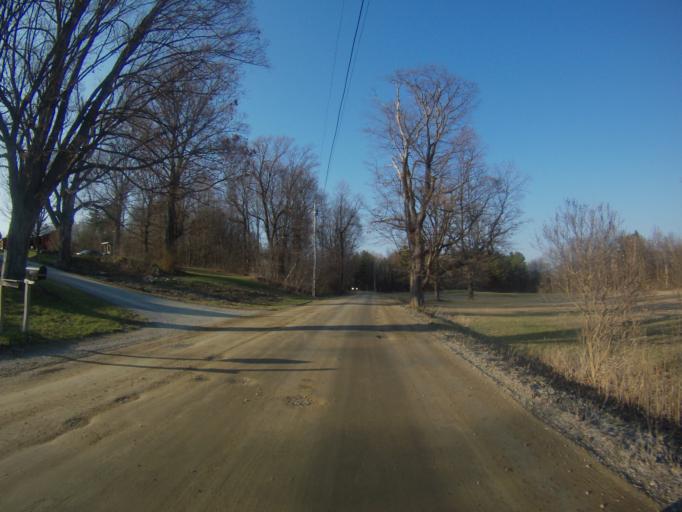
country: US
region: Vermont
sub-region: Addison County
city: Middlebury (village)
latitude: 44.0502
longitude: -73.1464
